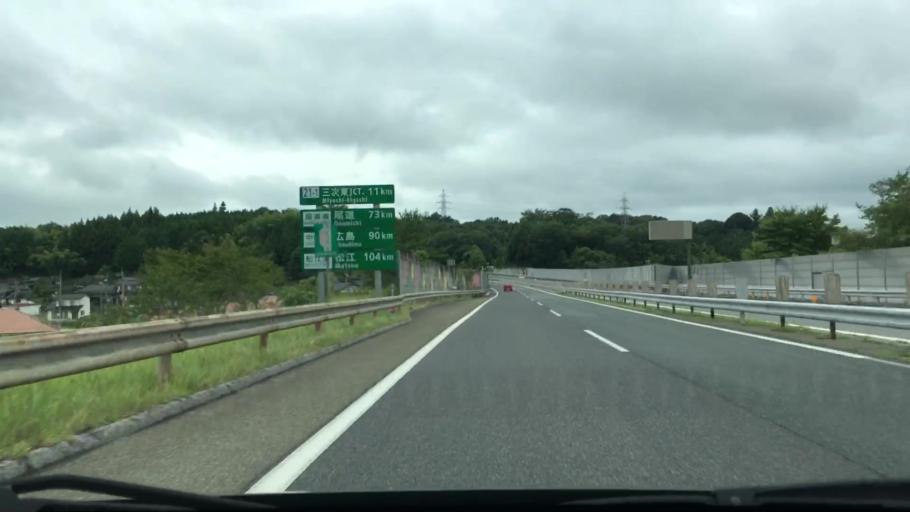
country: JP
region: Hiroshima
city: Shobara
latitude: 34.8460
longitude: 133.0179
